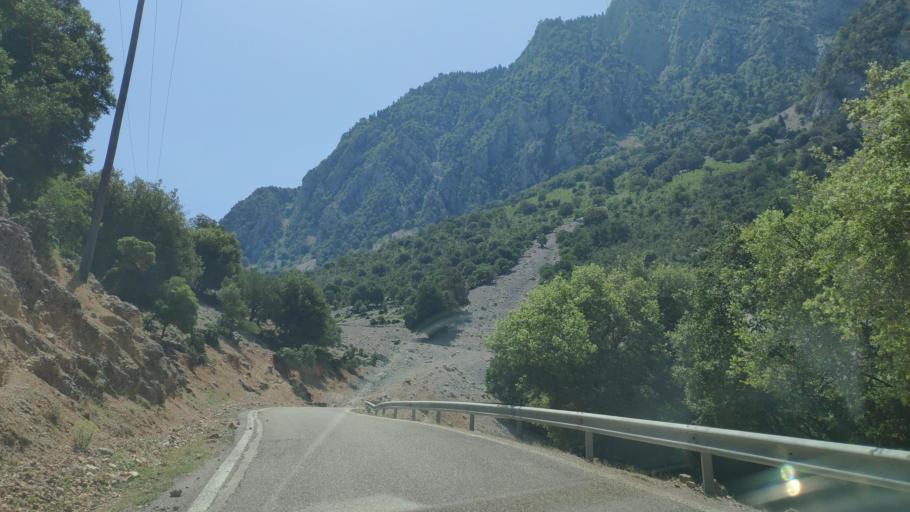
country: GR
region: West Greece
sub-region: Nomos Aitolias kai Akarnanias
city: Krikellos
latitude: 39.0218
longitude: 21.3370
